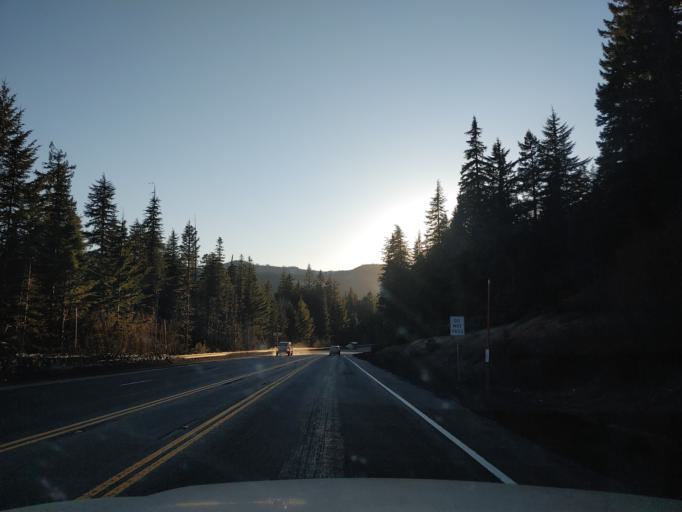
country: US
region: Oregon
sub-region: Lane County
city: Oakridge
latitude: 43.6109
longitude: -122.1192
